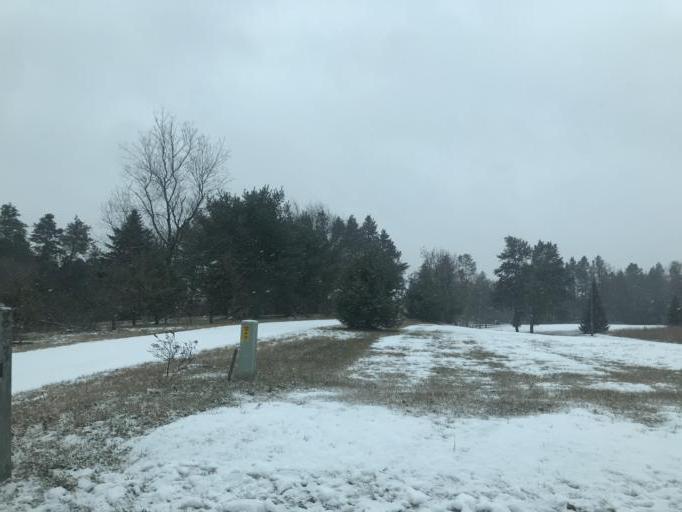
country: US
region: Wisconsin
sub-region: Marinette County
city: Peshtigo
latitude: 45.2801
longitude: -88.0398
